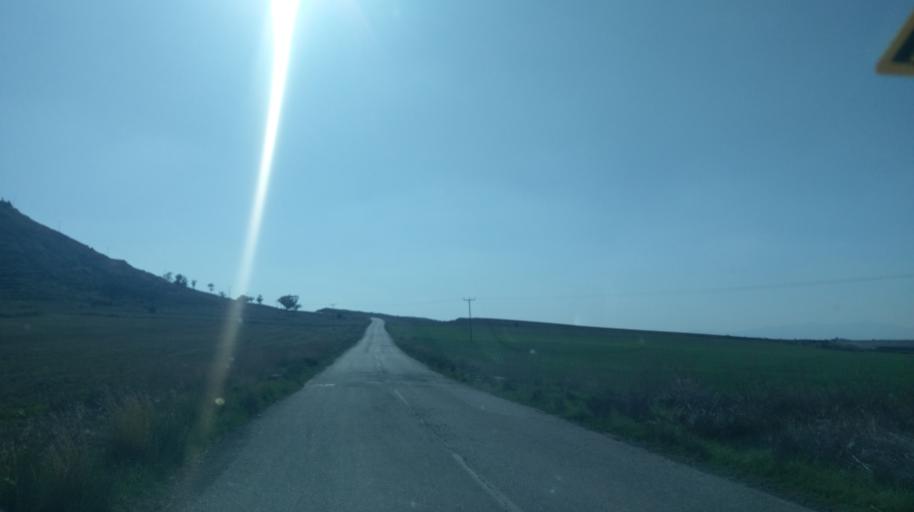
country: CY
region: Larnaka
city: Athienou
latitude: 35.0687
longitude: 33.4837
